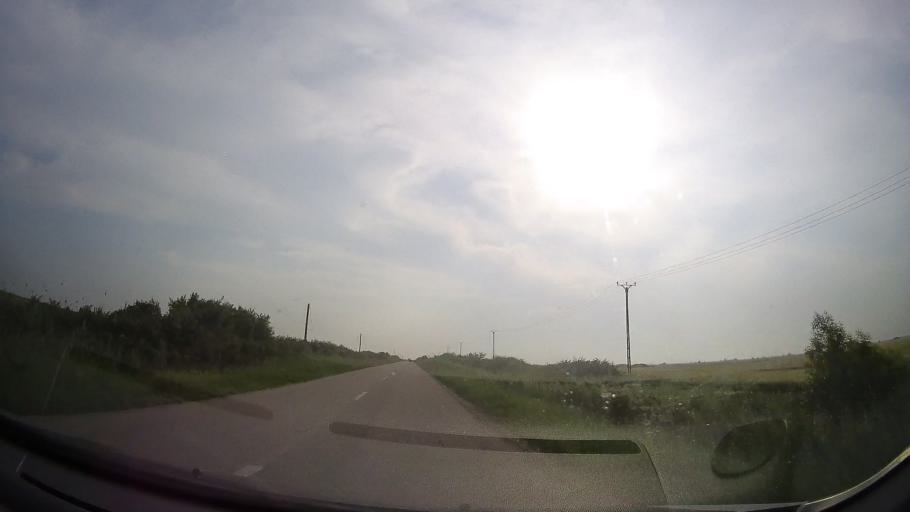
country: RO
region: Timis
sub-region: Comuna Foeni
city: Foeni
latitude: 45.5244
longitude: 20.9227
